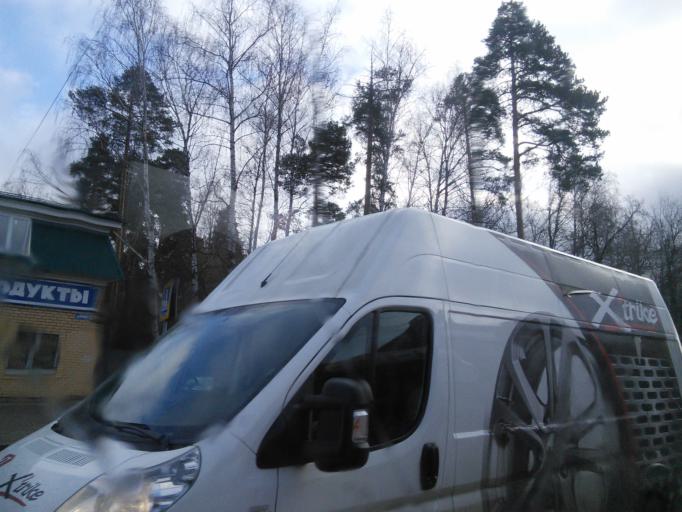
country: RU
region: Moskovskaya
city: Likino-Dulevo
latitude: 55.7081
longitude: 38.9578
